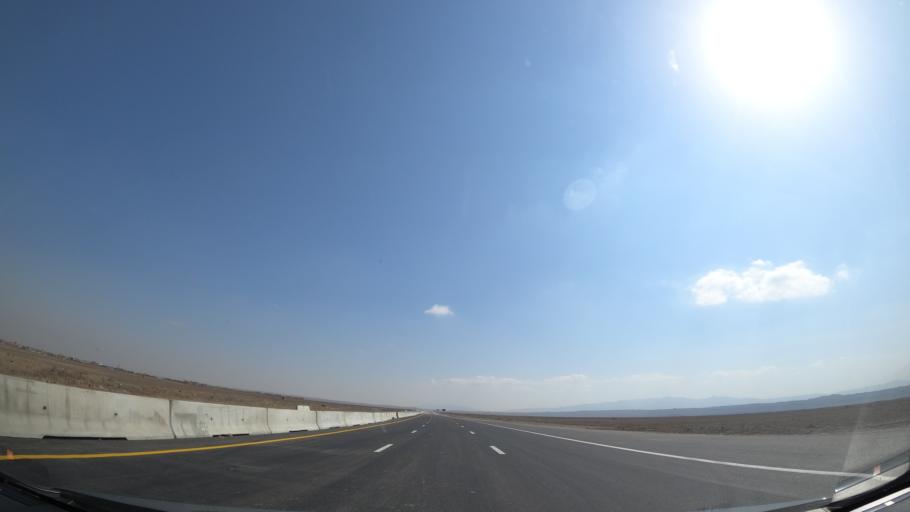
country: IR
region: Alborz
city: Nazarabad
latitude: 35.8420
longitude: 50.4853
